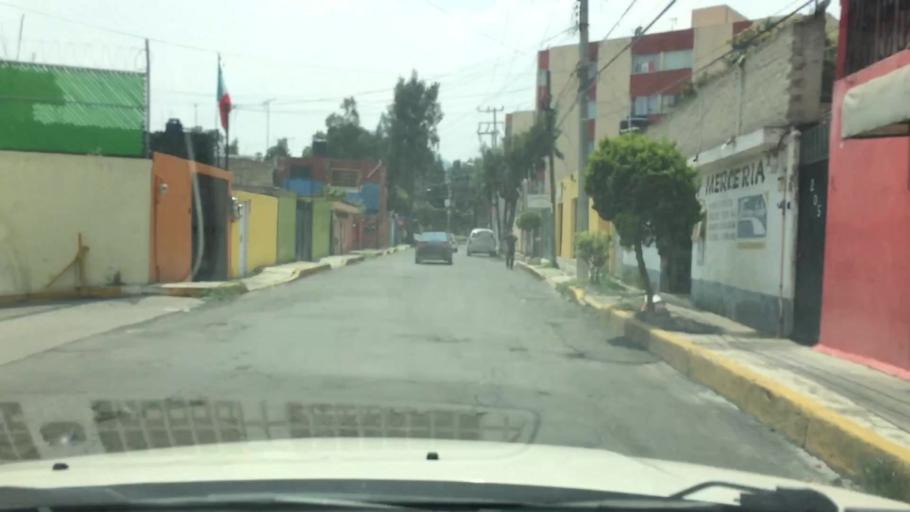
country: MX
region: Mexico City
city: Xochimilco
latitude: 19.2749
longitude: -99.1298
